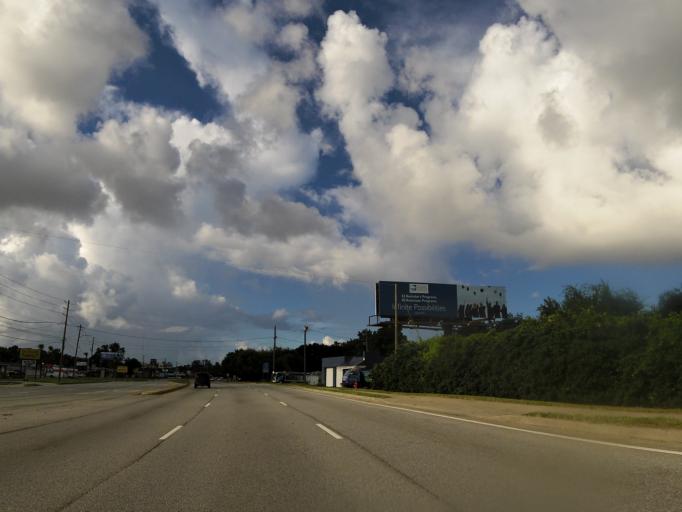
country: US
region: Georgia
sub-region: Glynn County
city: Brunswick
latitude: 31.1664
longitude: -81.4747
